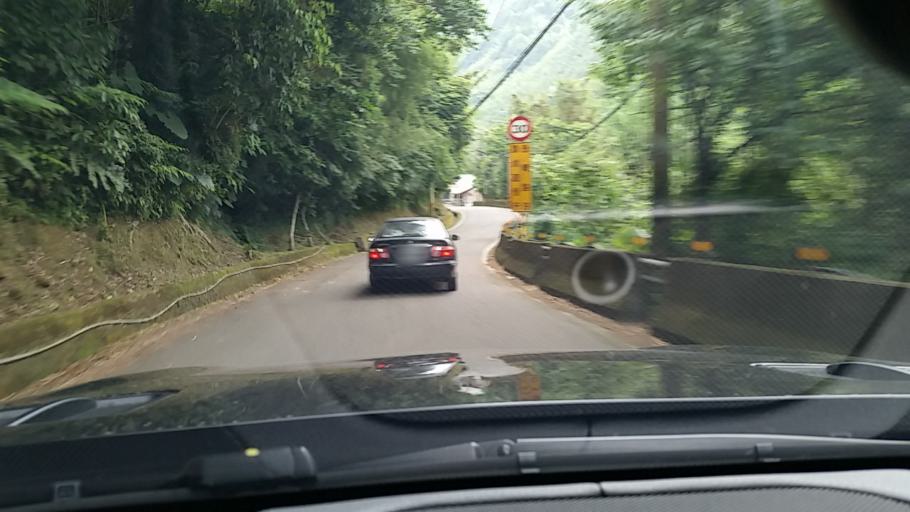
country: TW
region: Taiwan
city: Daxi
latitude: 24.7982
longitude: 121.3028
